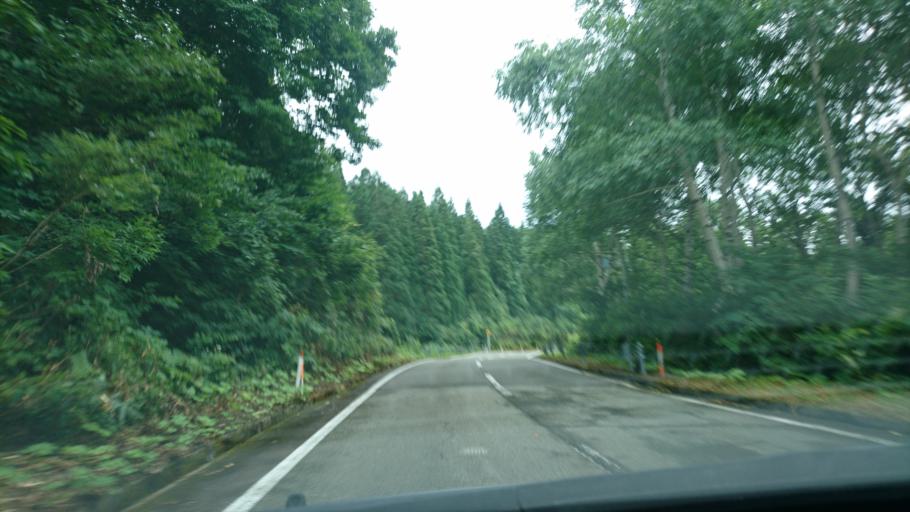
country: JP
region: Akita
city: Yuzawa
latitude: 38.9731
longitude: 140.7230
